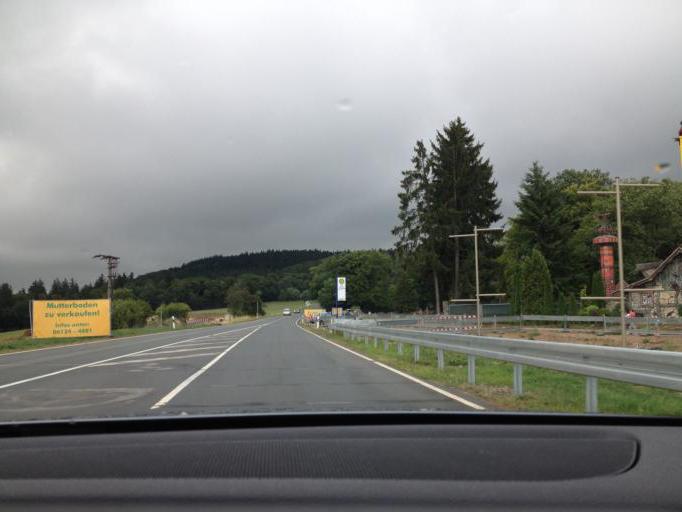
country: DE
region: Hesse
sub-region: Regierungsbezirk Darmstadt
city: Schlangenbad
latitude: 50.1165
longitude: 8.1112
